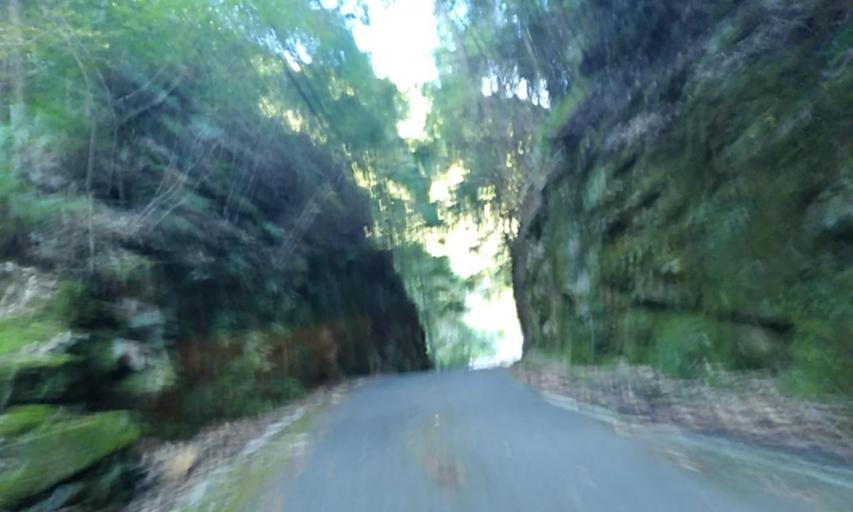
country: JP
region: Wakayama
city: Shingu
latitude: 33.9081
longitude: 135.9957
